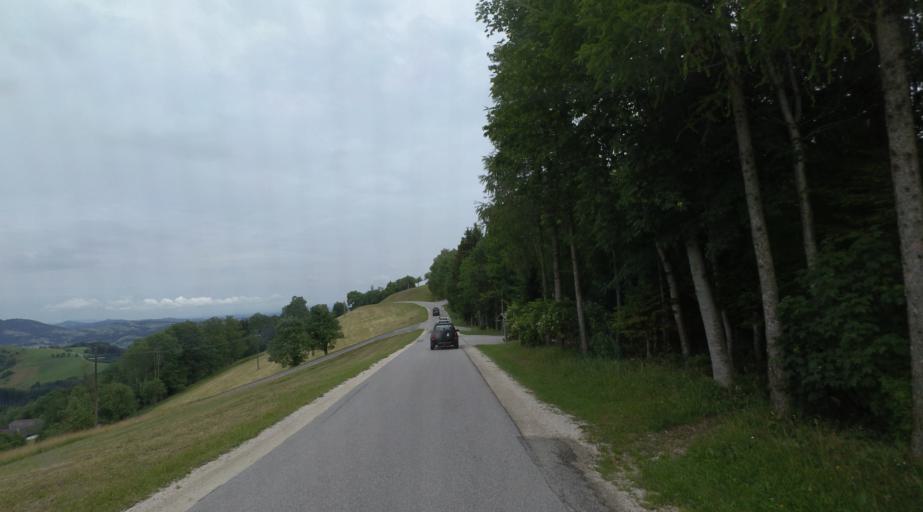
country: AT
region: Upper Austria
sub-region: Politischer Bezirk Kirchdorf an der Krems
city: Micheldorf in Oberoesterreich
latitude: 47.9354
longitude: 14.1690
